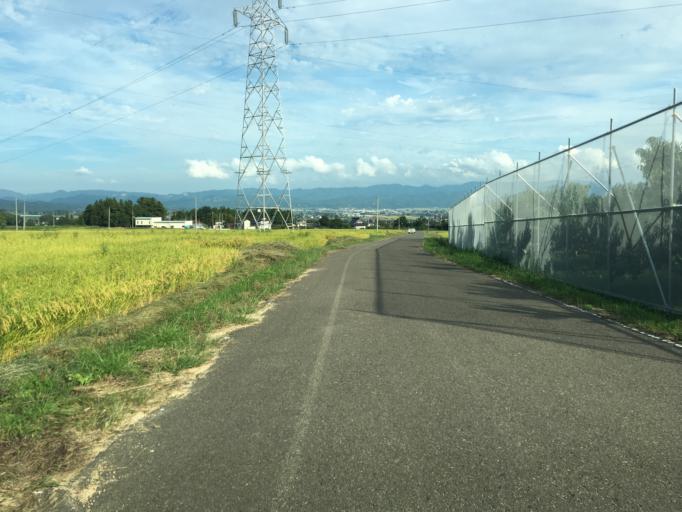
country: JP
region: Fukushima
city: Hobaramachi
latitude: 37.8813
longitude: 140.5205
